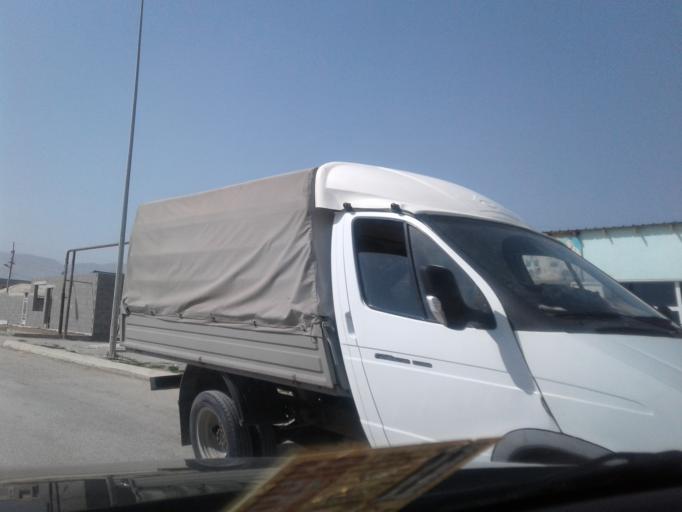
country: TM
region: Ahal
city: Abadan
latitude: 38.1594
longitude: 57.9768
